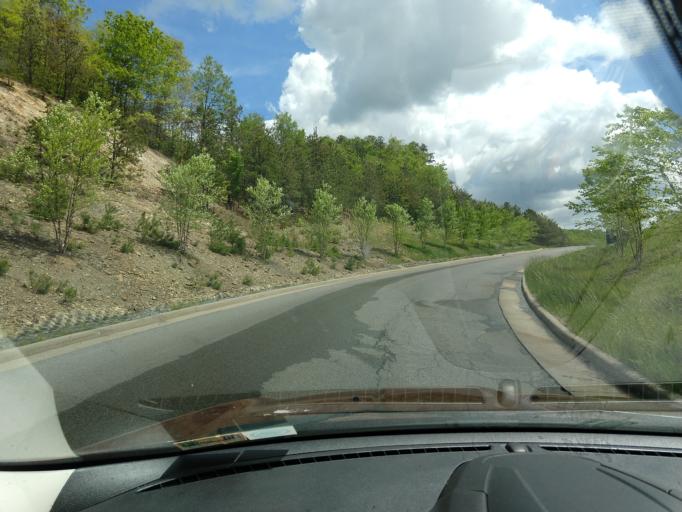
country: US
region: West Virginia
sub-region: Mercer County
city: Bluefield
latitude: 37.2552
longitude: -81.2393
